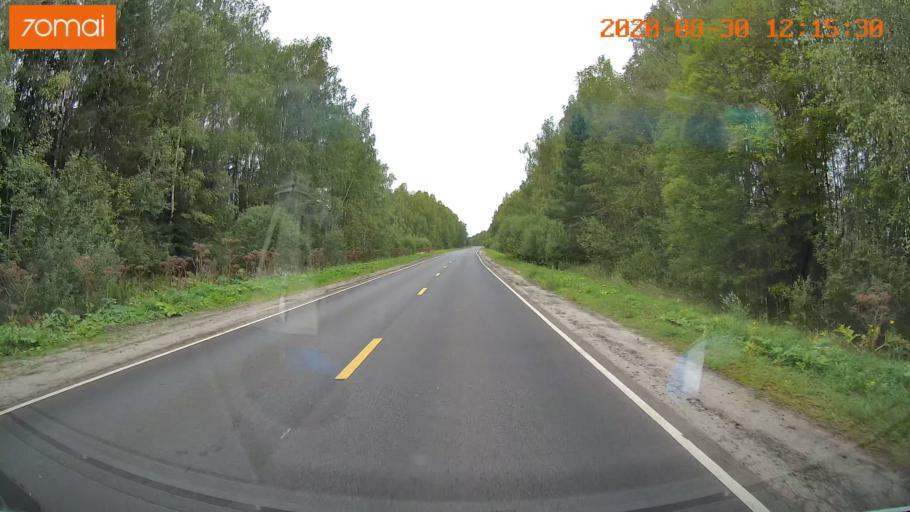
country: RU
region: Ivanovo
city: Yur'yevets
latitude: 57.3175
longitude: 43.0280
